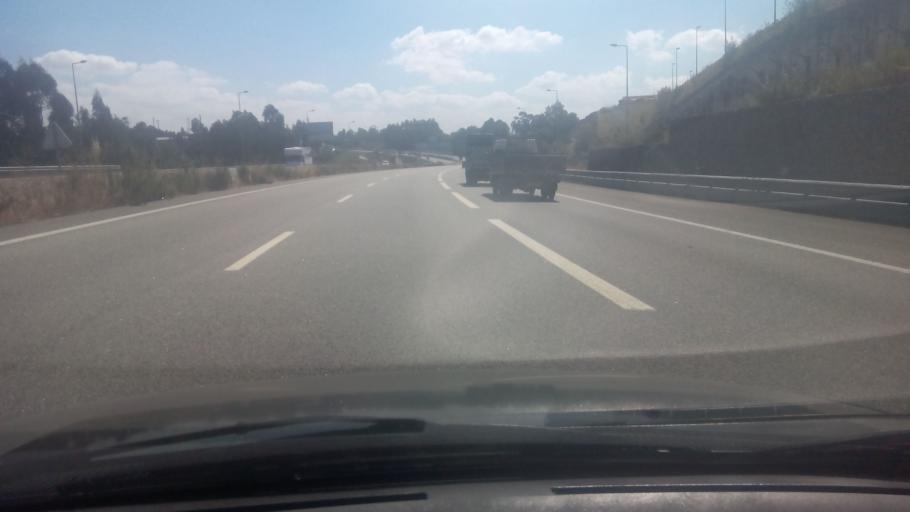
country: PT
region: Porto
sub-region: Valongo
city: Campo
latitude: 41.1793
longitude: -8.4439
